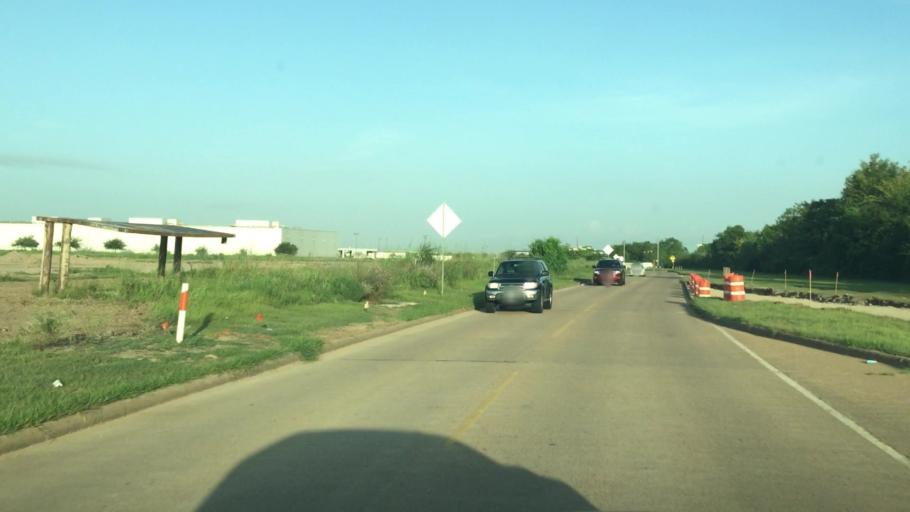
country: US
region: Texas
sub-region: Harris County
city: Hudson
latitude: 29.9427
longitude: -95.4800
